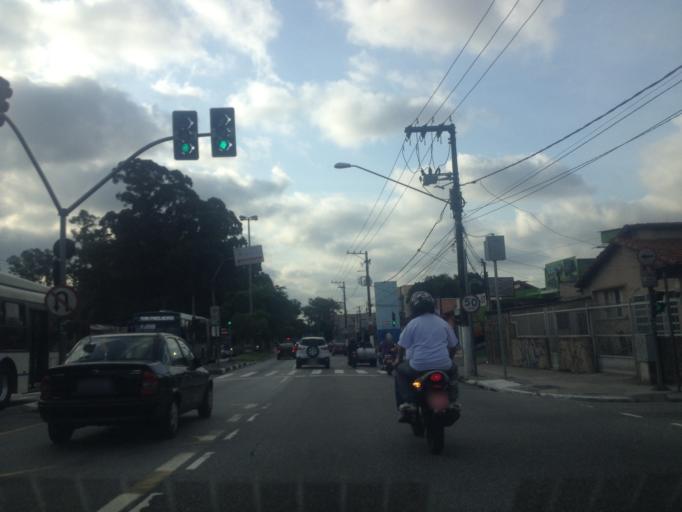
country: BR
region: Sao Paulo
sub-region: Diadema
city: Diadema
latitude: -23.7152
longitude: -46.7067
